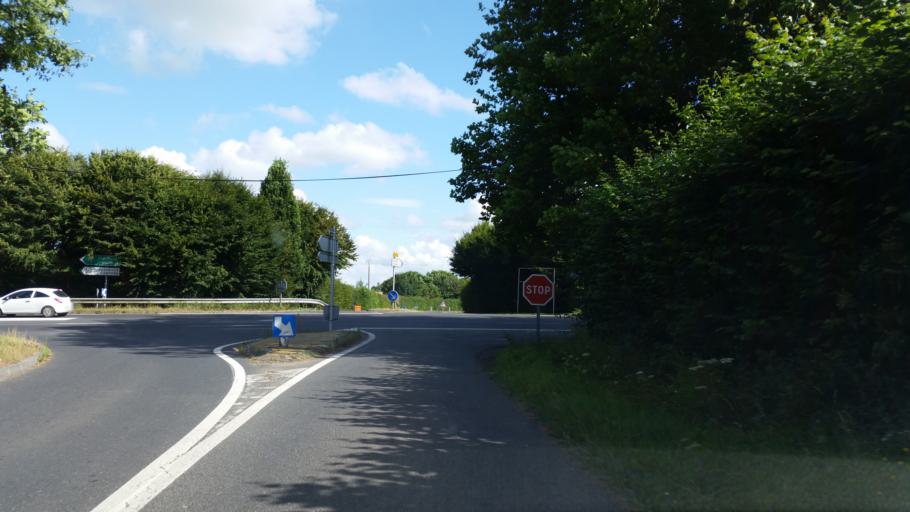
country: FR
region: Lower Normandy
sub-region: Departement du Calvados
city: Bavent
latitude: 49.2386
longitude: -0.1901
